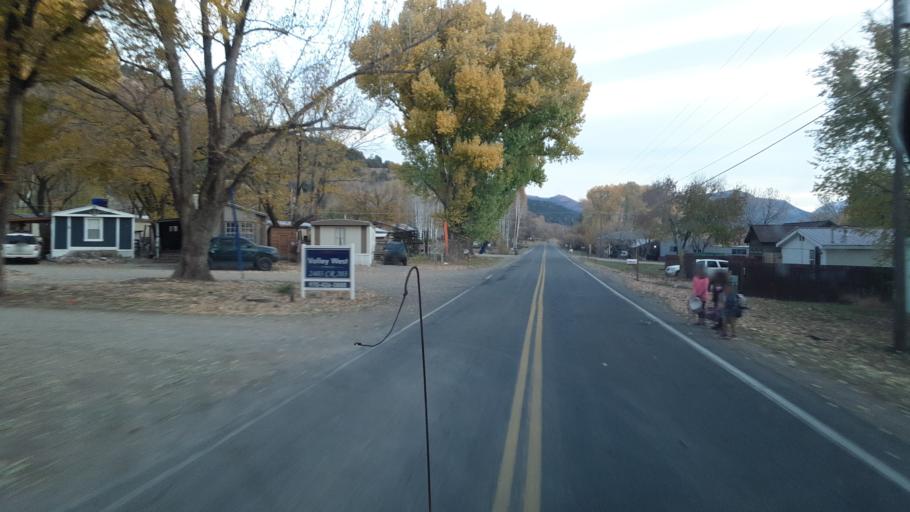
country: US
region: Colorado
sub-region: La Plata County
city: Durango
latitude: 37.3344
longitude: -107.8550
